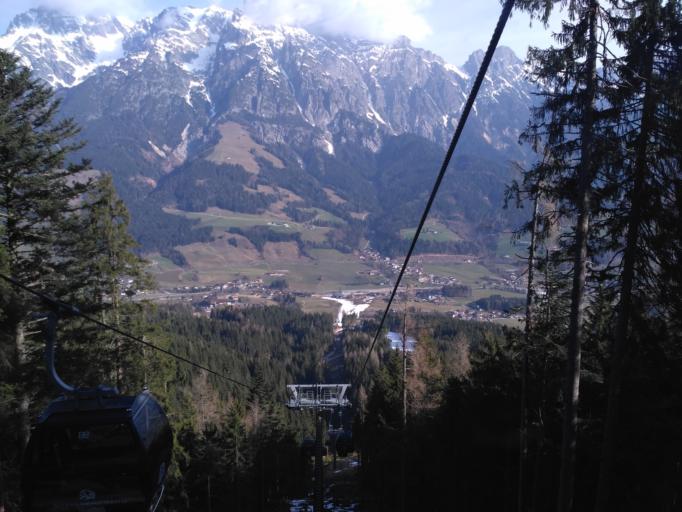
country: AT
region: Salzburg
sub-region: Politischer Bezirk Zell am See
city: Leogang
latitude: 47.4228
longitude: 12.7312
